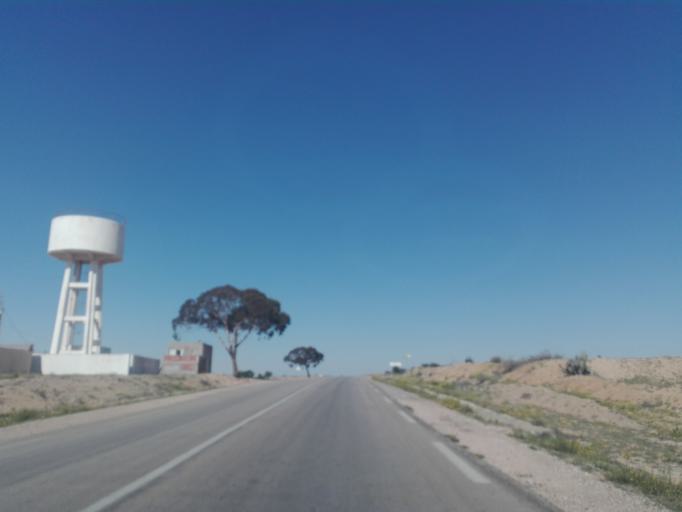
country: TN
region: Safaqis
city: Bi'r `Ali Bin Khalifah
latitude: 34.7399
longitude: 10.3952
